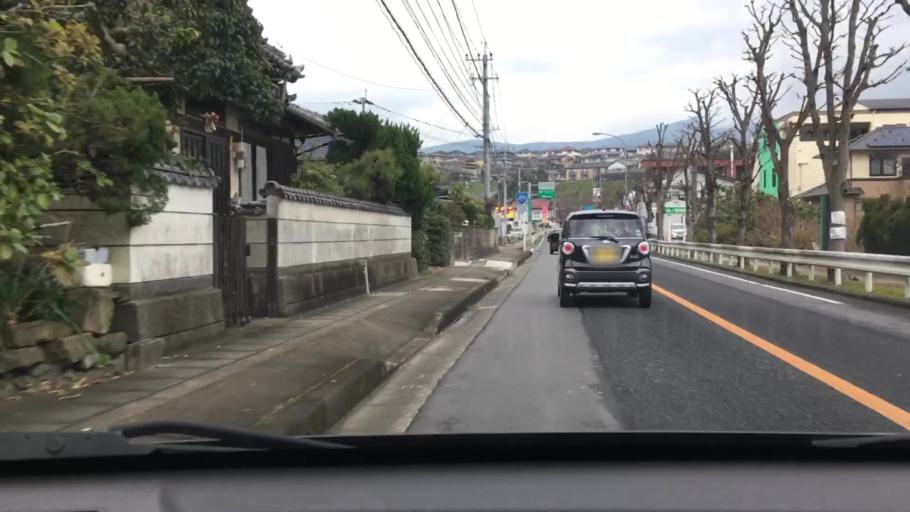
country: JP
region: Nagasaki
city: Sasebo
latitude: 33.1295
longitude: 129.7923
